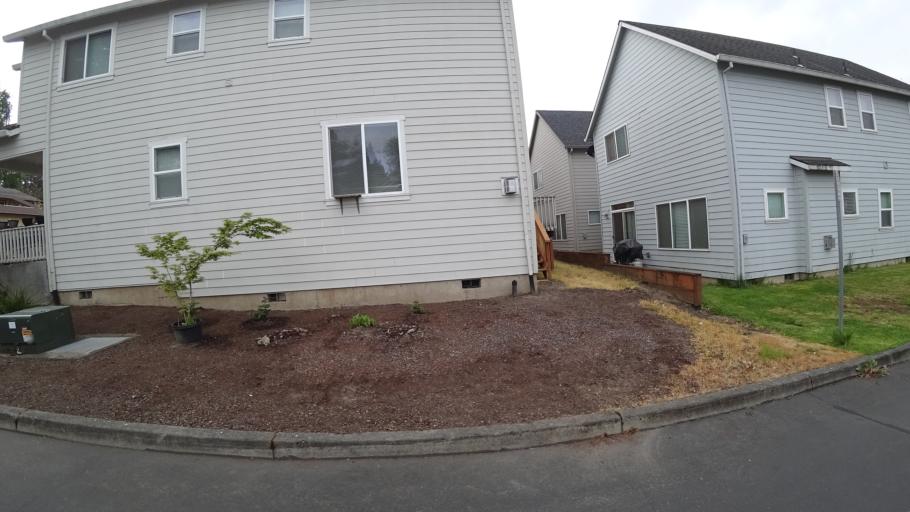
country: US
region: Oregon
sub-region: Washington County
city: Hillsboro
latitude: 45.5239
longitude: -122.9996
